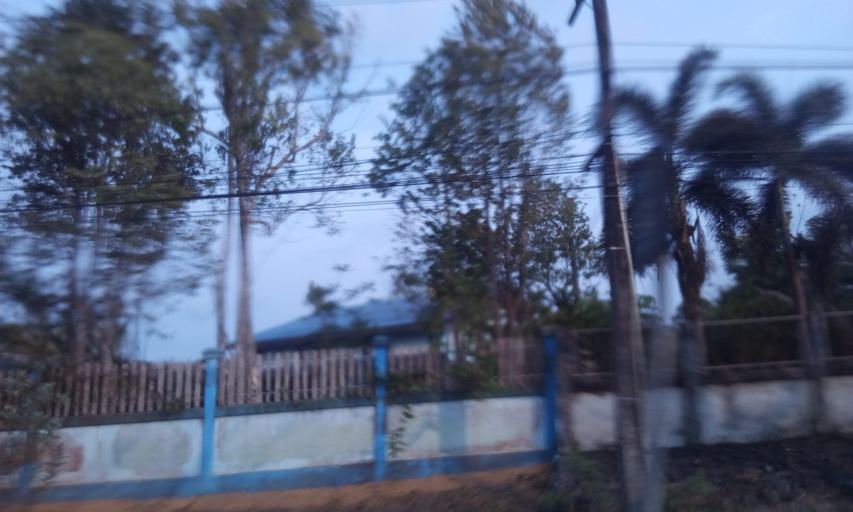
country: TH
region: Trat
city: Khao Saming
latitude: 12.2945
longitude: 102.3330
